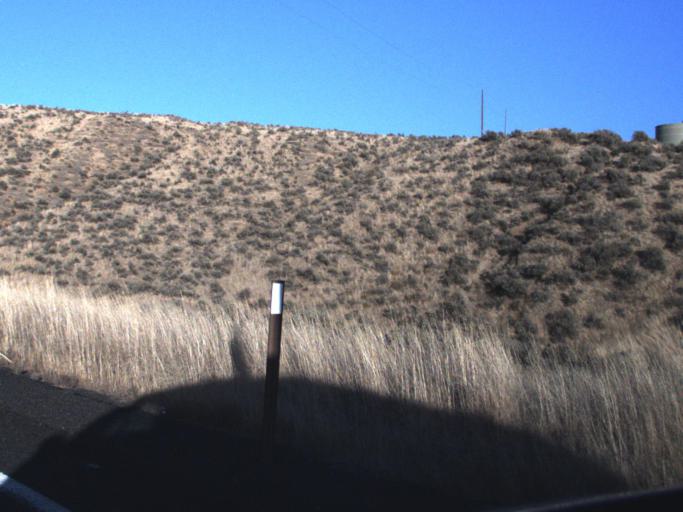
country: US
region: Washington
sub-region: Franklin County
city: Connell
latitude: 46.6480
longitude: -118.5568
